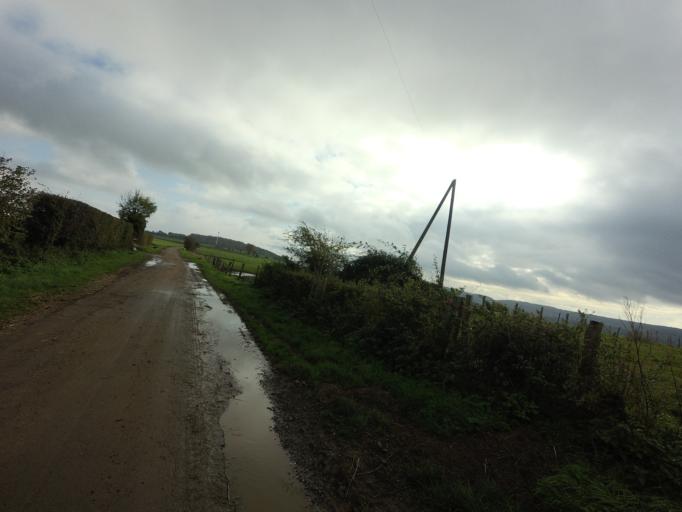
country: NL
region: Limburg
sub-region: Gemeente Vaals
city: Vaals
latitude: 50.7943
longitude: 6.0012
